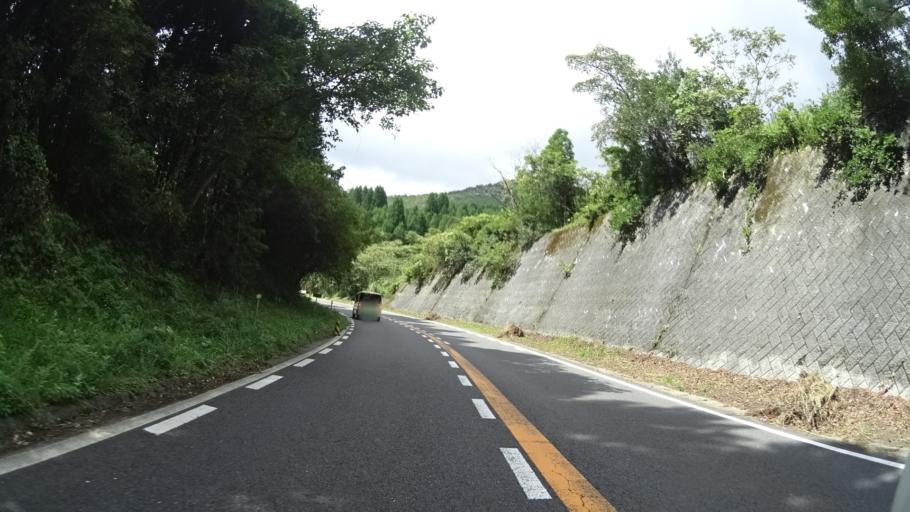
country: JP
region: Oita
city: Tsukawaki
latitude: 33.2106
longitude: 131.2969
